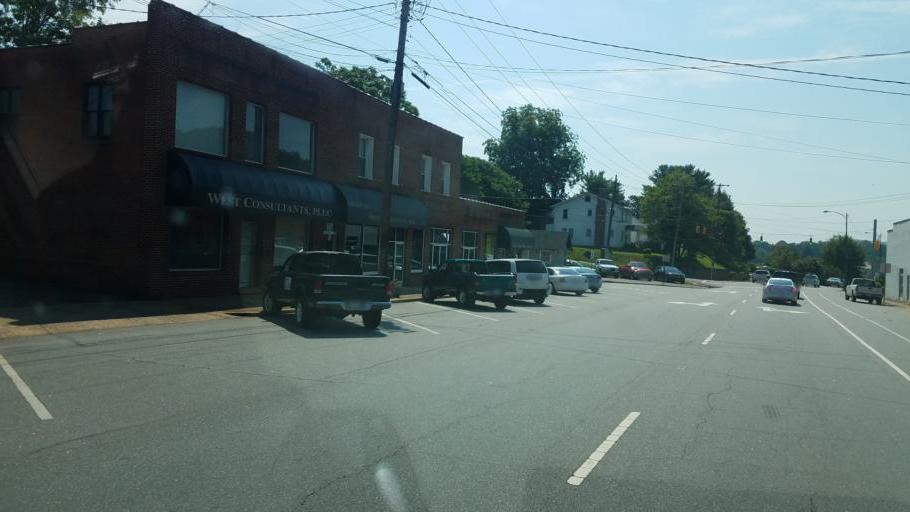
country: US
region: North Carolina
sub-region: Burke County
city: Morganton
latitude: 35.7429
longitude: -81.6843
